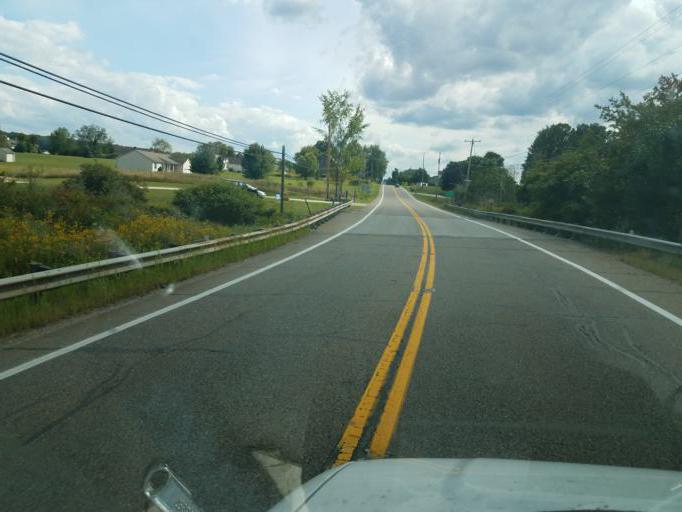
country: US
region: Ohio
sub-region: Portage County
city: Ravenna
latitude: 41.0614
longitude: -81.2473
